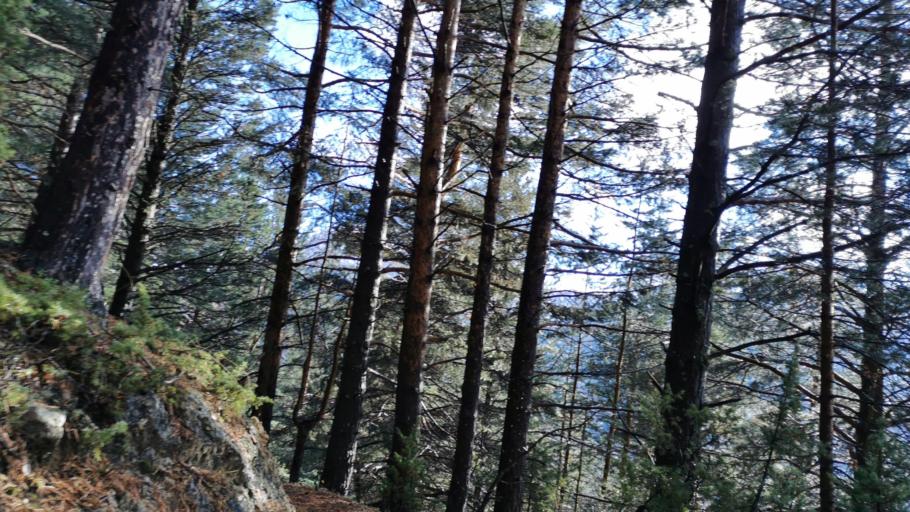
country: IT
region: Piedmont
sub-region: Provincia di Torino
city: Bardonecchia
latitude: 45.0251
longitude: 6.6237
